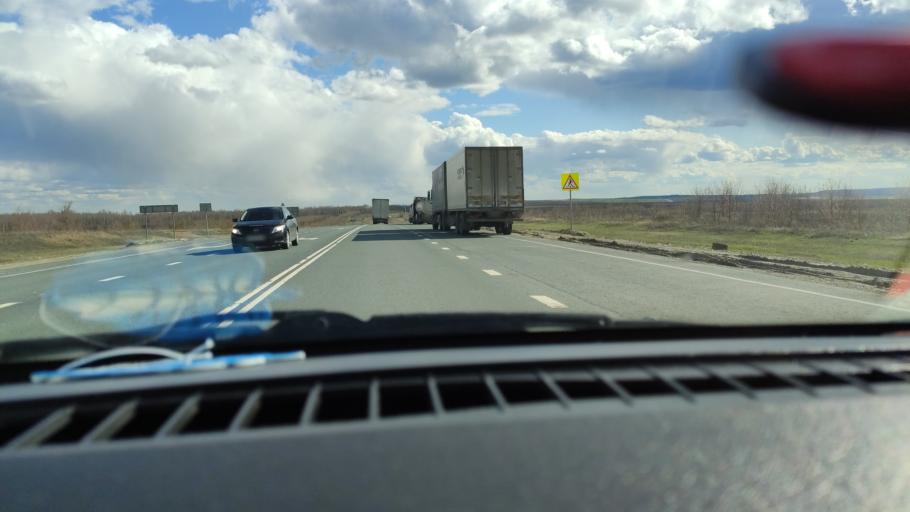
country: RU
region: Saratov
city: Alekseyevka
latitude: 52.2874
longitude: 47.9304
